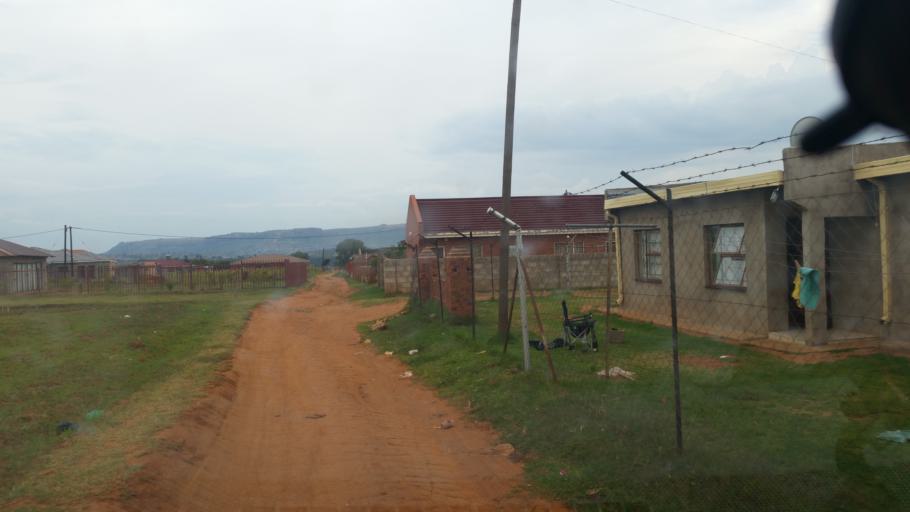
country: LS
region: Maseru
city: Maseru
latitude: -29.4221
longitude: 27.5673
